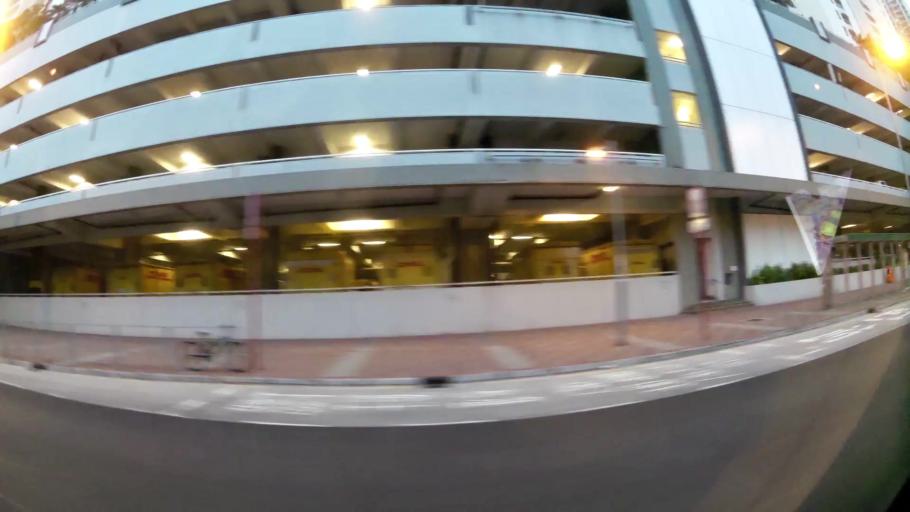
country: HK
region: Sham Shui Po
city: Sham Shui Po
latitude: 22.3285
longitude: 114.1535
